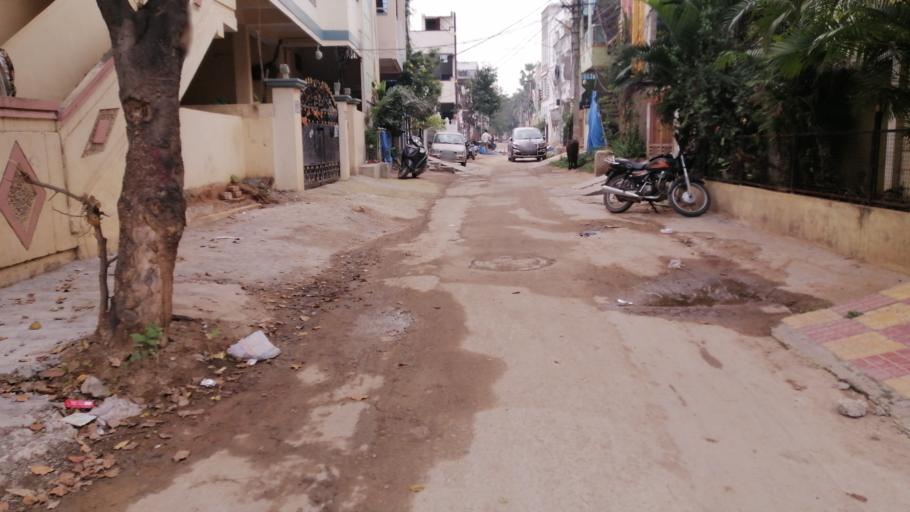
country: IN
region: Telangana
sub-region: Rangareddi
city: Secunderabad
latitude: 17.4837
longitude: 78.5813
